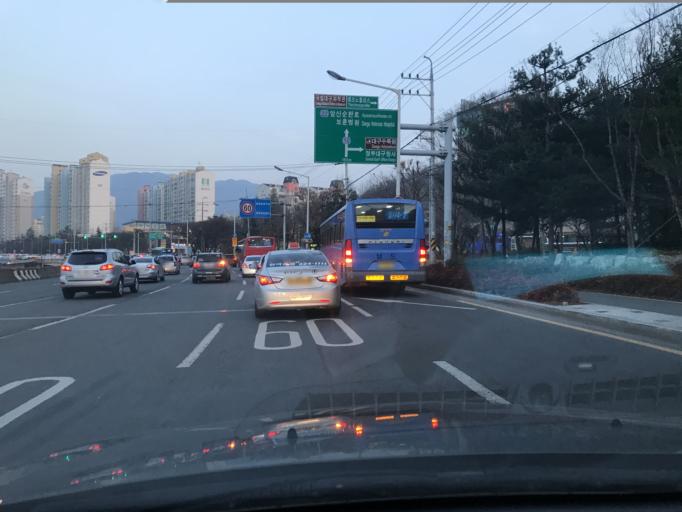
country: KR
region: Daegu
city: Hwawon
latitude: 35.8081
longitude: 128.5186
